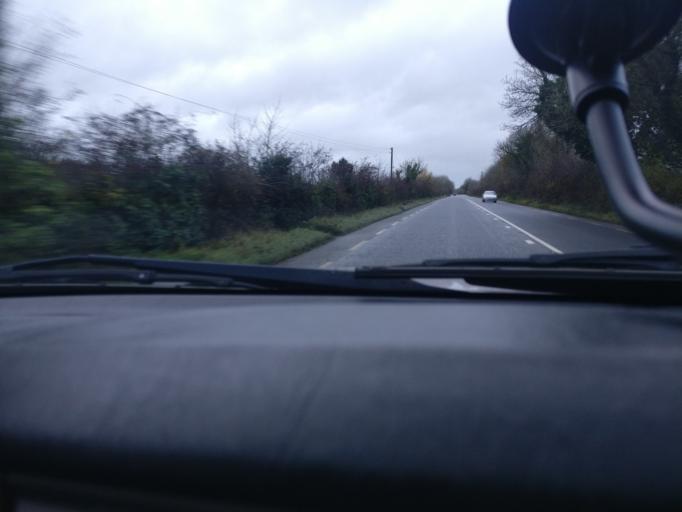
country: IE
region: Leinster
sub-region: Kildare
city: Kilcock
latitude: 53.4127
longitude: -6.7146
